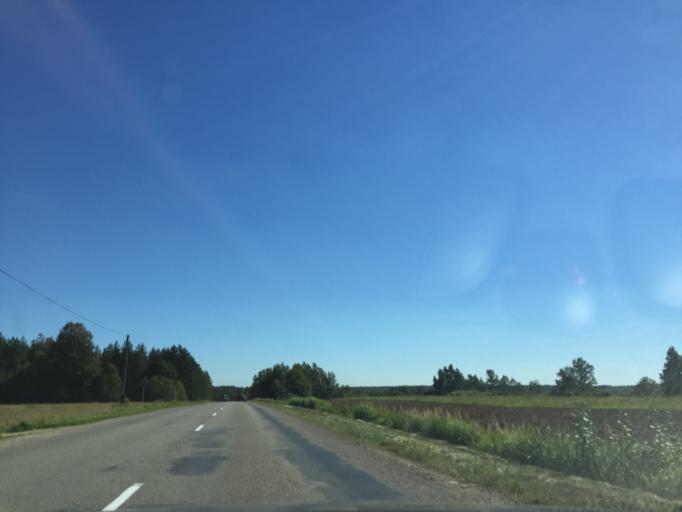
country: LV
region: Akniste
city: Akniste
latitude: 56.1322
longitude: 25.8260
